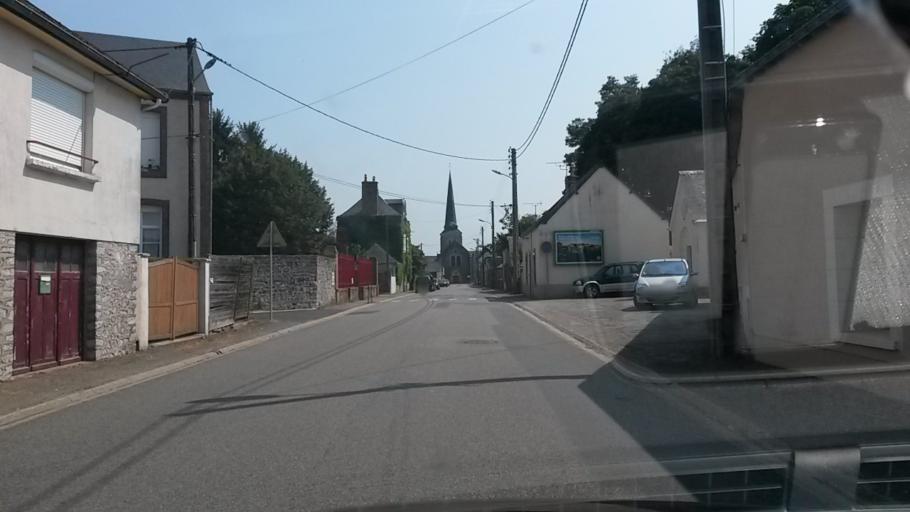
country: FR
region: Pays de la Loire
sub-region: Departement de la Mayenne
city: Soulge-sur-Ouette
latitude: 48.0181
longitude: -0.5844
